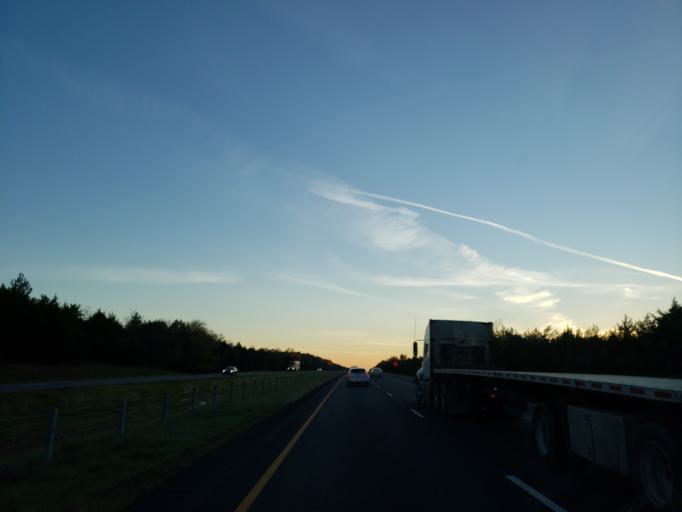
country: US
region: Alabama
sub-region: Sumter County
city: Livingston
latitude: 32.6697
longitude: -88.1736
